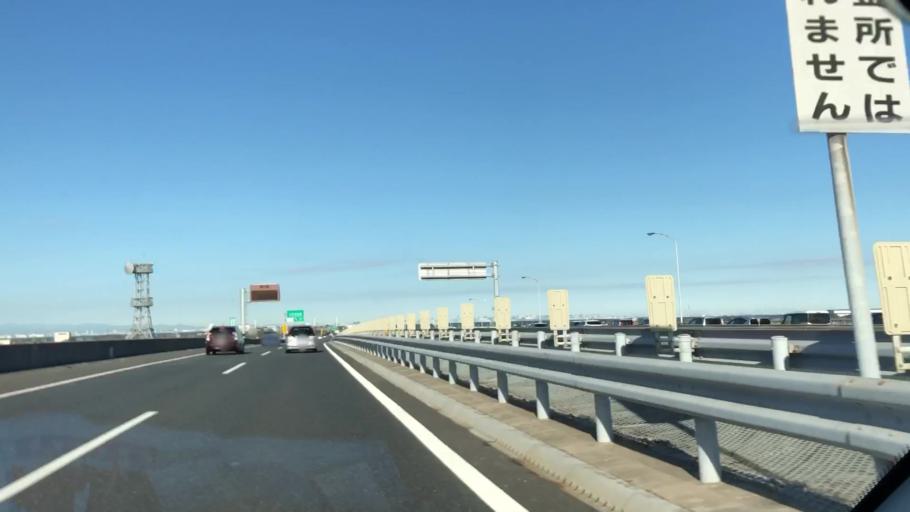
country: JP
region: Chiba
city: Kisarazu
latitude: 35.4249
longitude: 139.9320
